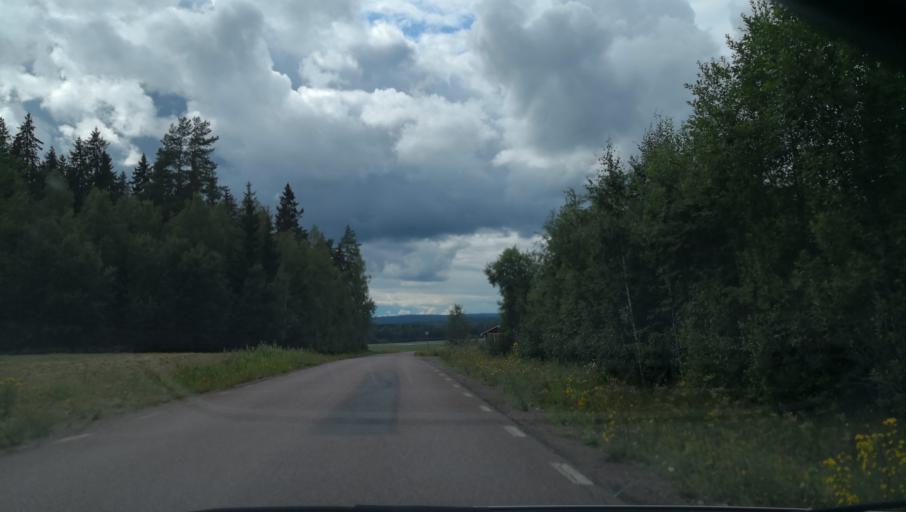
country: SE
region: Dalarna
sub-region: Borlange Kommun
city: Ornas
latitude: 60.4418
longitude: 15.5955
